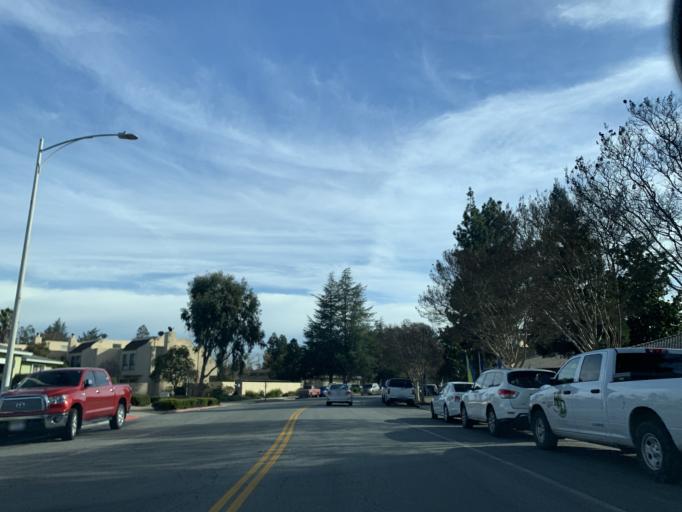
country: US
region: California
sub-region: Santa Clara County
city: Gilroy
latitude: 37.0155
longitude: -121.5944
